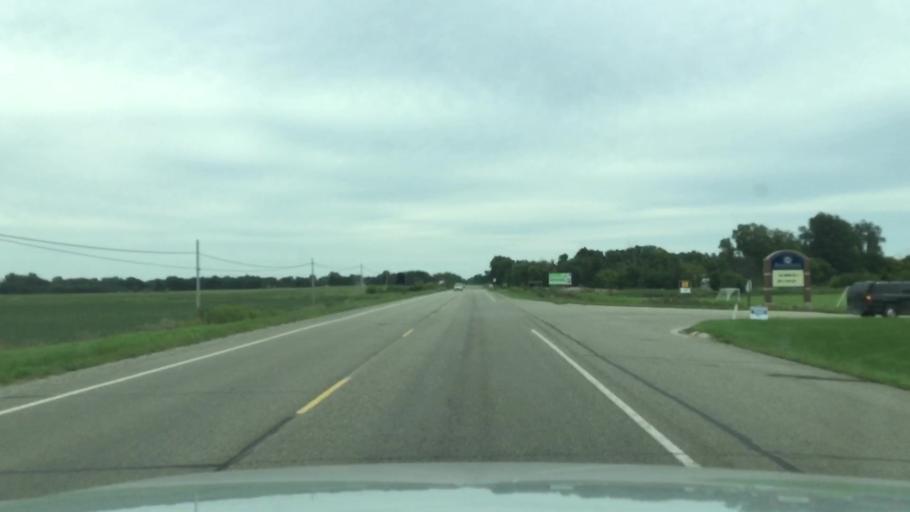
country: US
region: Michigan
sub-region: Shiawassee County
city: Durand
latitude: 42.9254
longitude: -83.9786
